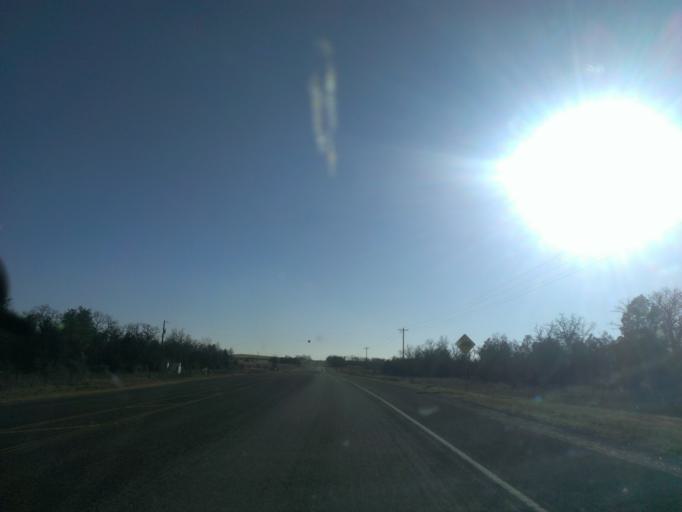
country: US
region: Texas
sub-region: Bastrop County
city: Elgin
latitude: 30.3731
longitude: -97.2601
